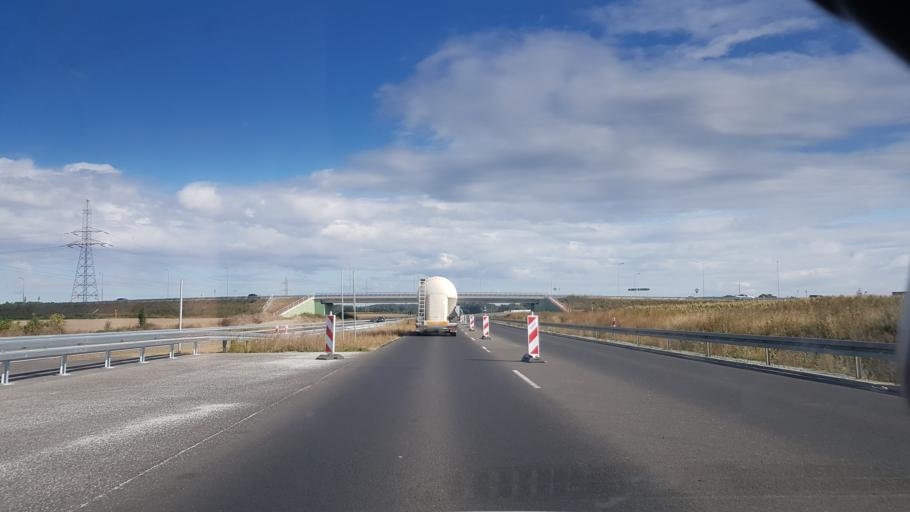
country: PL
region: Greater Poland Voivodeship
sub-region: Powiat poznanski
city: Steszew
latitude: 52.2845
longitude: 16.6731
